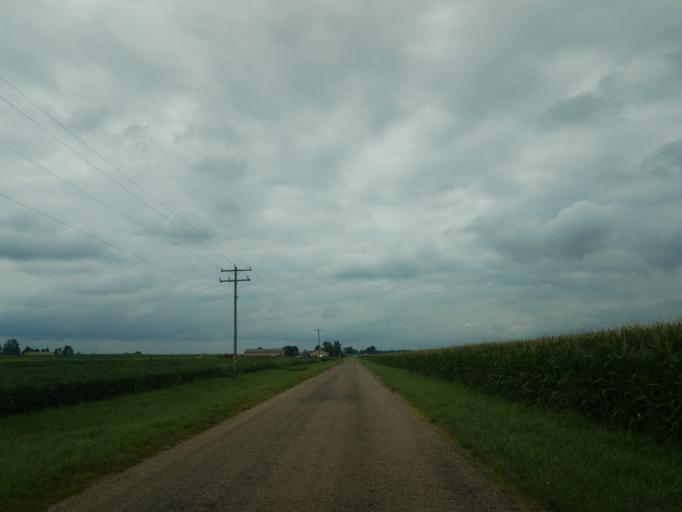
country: US
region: Illinois
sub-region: McLean County
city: Twin Grove
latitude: 40.4354
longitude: -89.0625
